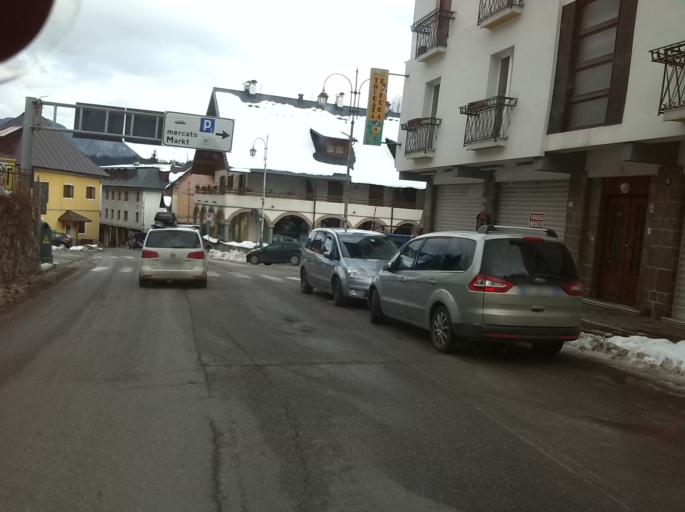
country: IT
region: Friuli Venezia Giulia
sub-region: Provincia di Udine
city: Tarvisio
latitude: 46.5039
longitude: 13.5832
